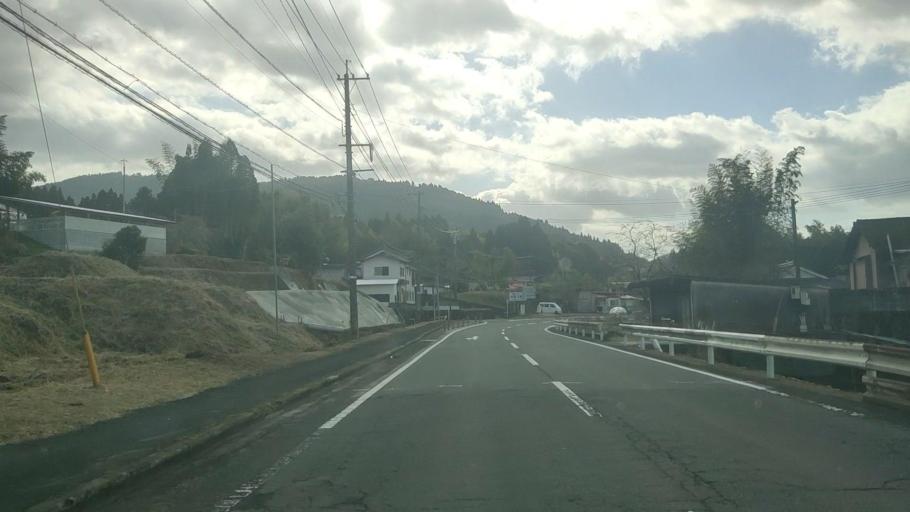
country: JP
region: Kagoshima
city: Okuchi-shinohara
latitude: 31.9919
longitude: 130.7478
